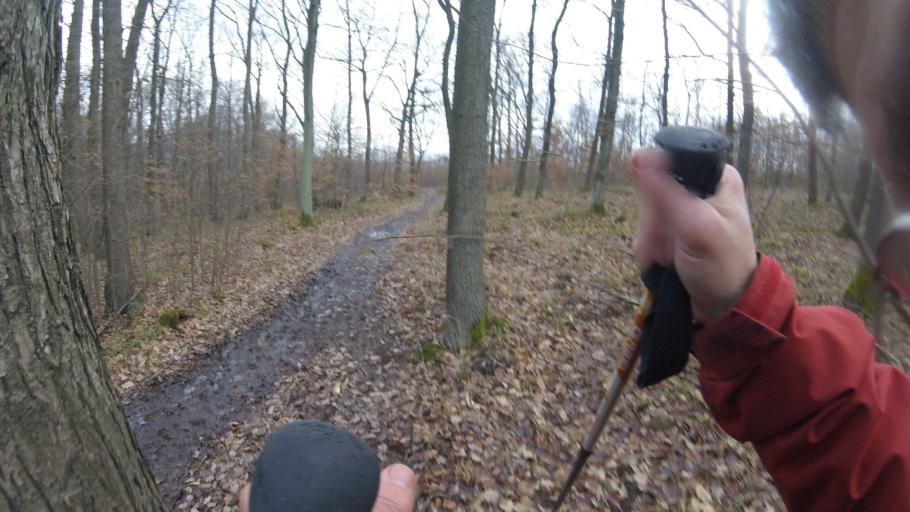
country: HU
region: Pest
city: Nagykovacsi
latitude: 47.6857
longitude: 18.9937
